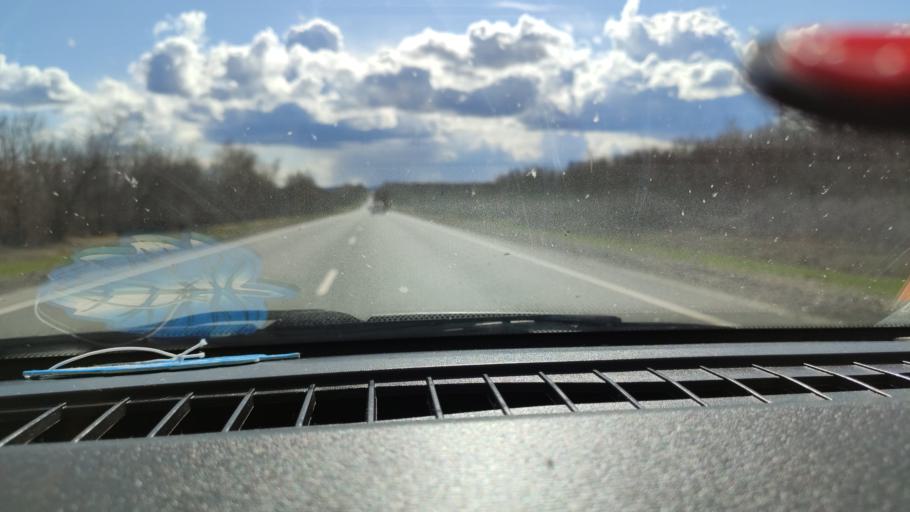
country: RU
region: Saratov
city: Khvalynsk
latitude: 52.6085
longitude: 48.1554
